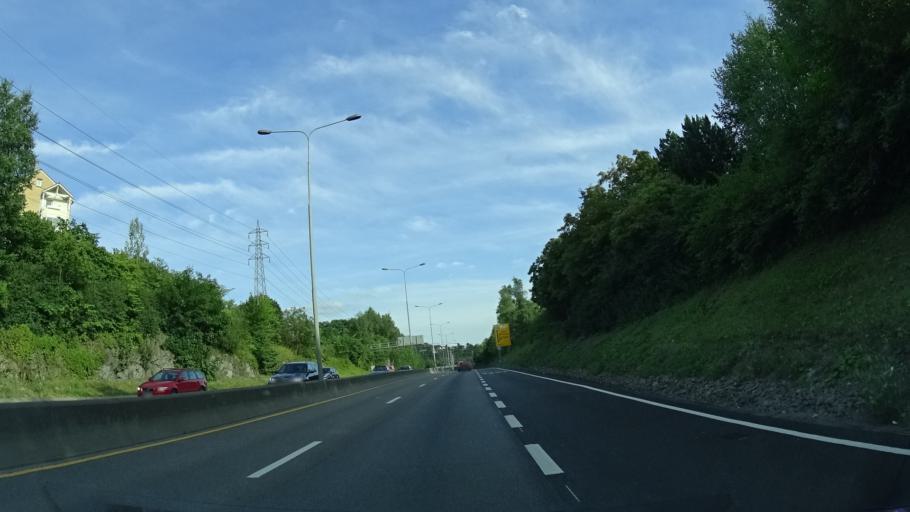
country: NO
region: Oslo
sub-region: Oslo
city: Oslo
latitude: 59.9162
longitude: 10.8130
